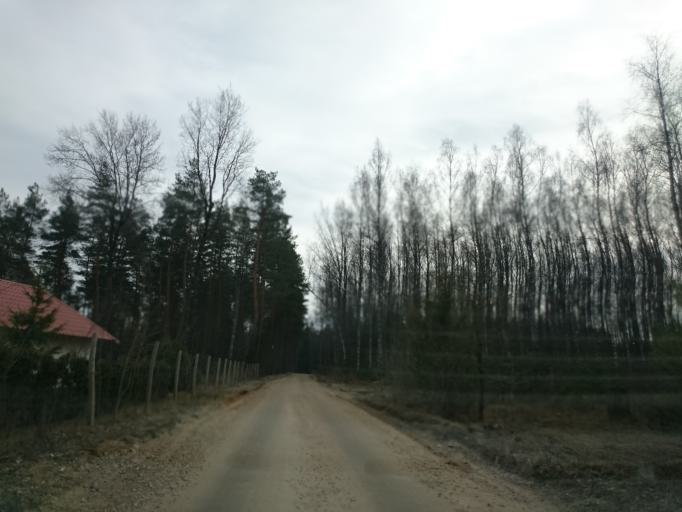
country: LV
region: Garkalne
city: Garkalne
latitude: 57.0251
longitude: 24.3863
